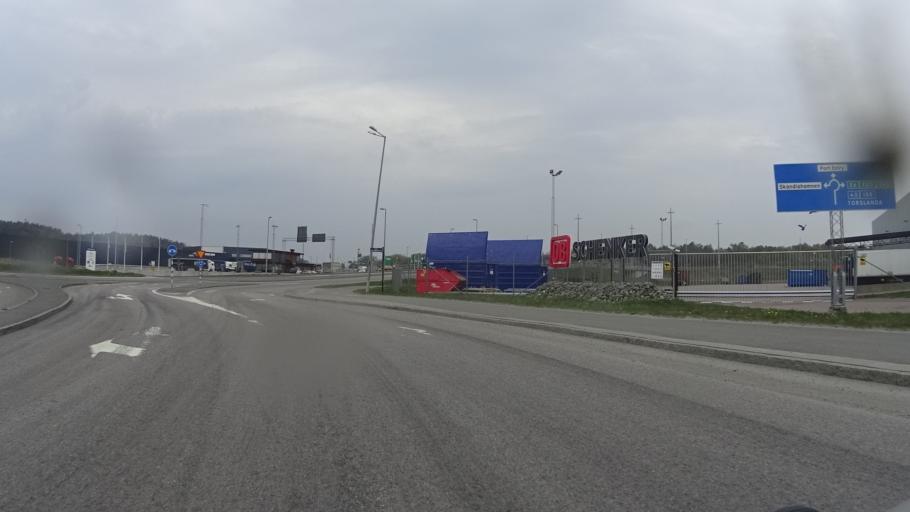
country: SE
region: Vaestra Goetaland
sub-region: Goteborg
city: Majorna
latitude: 57.7015
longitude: 11.8613
